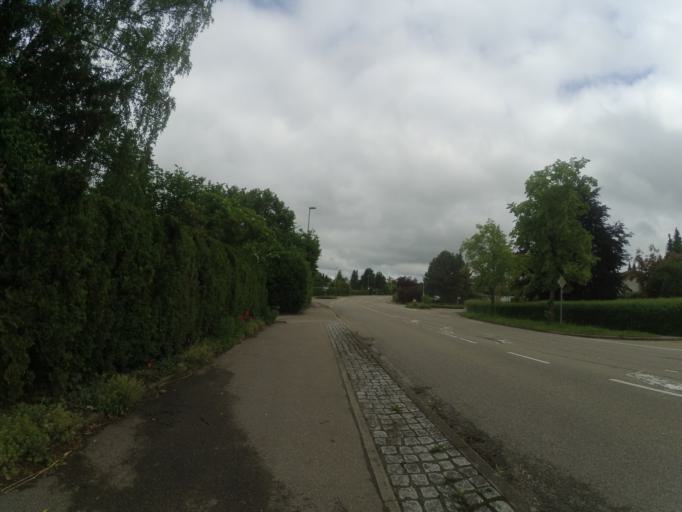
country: DE
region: Baden-Wuerttemberg
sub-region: Tuebingen Region
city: Bernstadt
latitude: 48.4947
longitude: 10.0267
